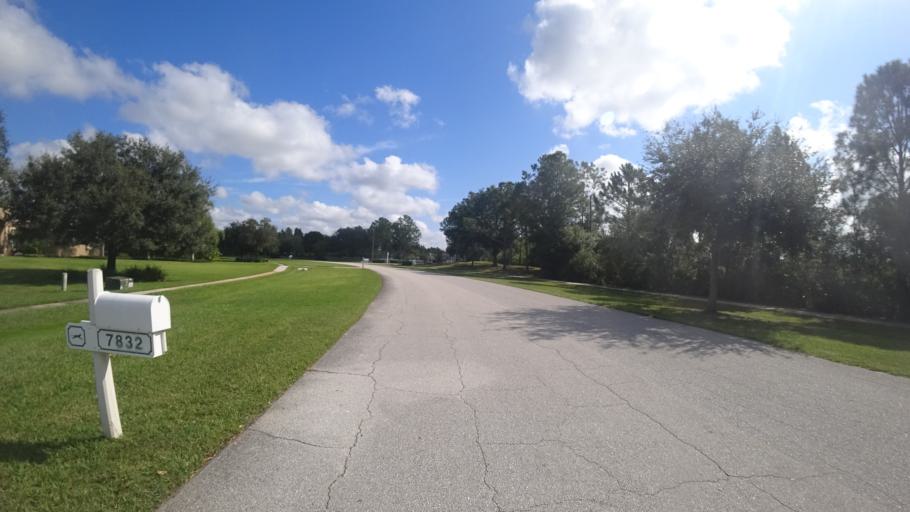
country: US
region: Florida
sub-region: Sarasota County
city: Fruitville
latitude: 27.3976
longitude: -82.3108
